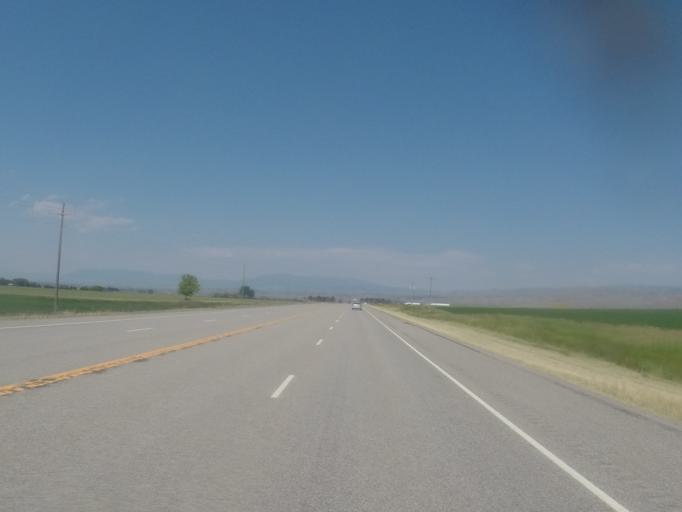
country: US
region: Montana
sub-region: Broadwater County
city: Townsend
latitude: 46.1269
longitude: -111.4912
